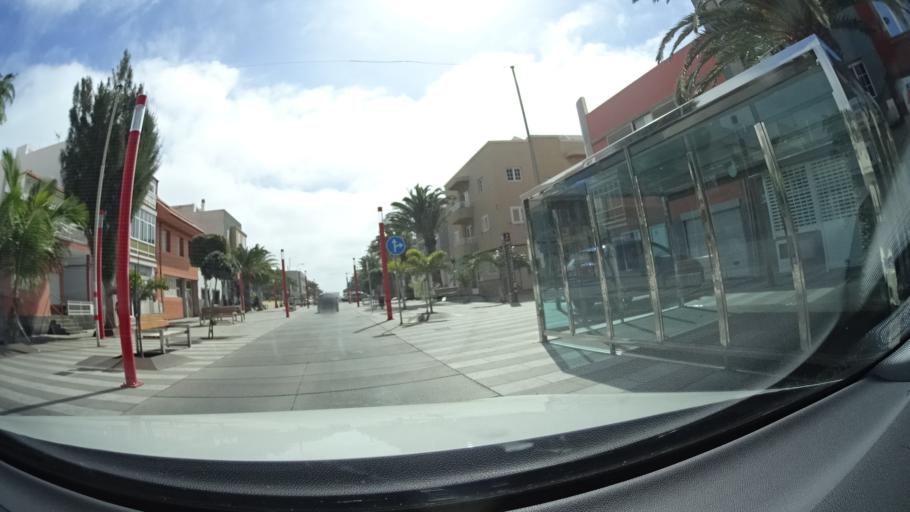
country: ES
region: Canary Islands
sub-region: Provincia de Las Palmas
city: Cruce de Arinaga
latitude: 27.8574
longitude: -15.3957
